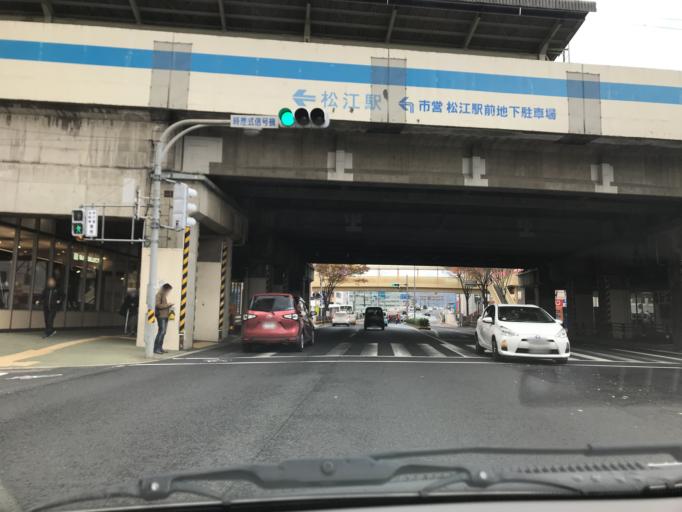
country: JP
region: Shimane
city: Matsue-shi
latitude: 35.4638
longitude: 133.0652
